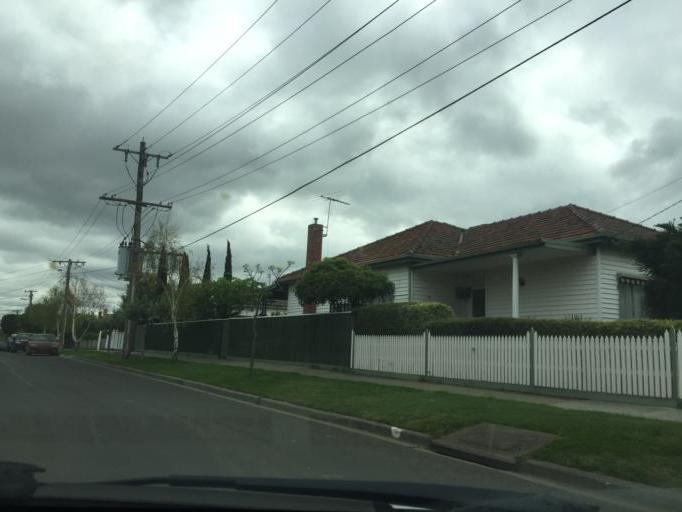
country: AU
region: Victoria
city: Spotswood
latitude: -37.8225
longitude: 144.8784
